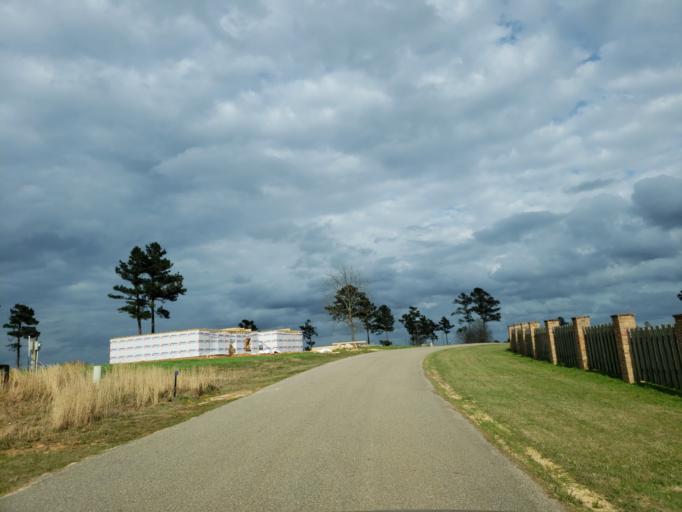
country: US
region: Mississippi
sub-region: Jones County
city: Ellisville
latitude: 31.5580
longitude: -89.2568
